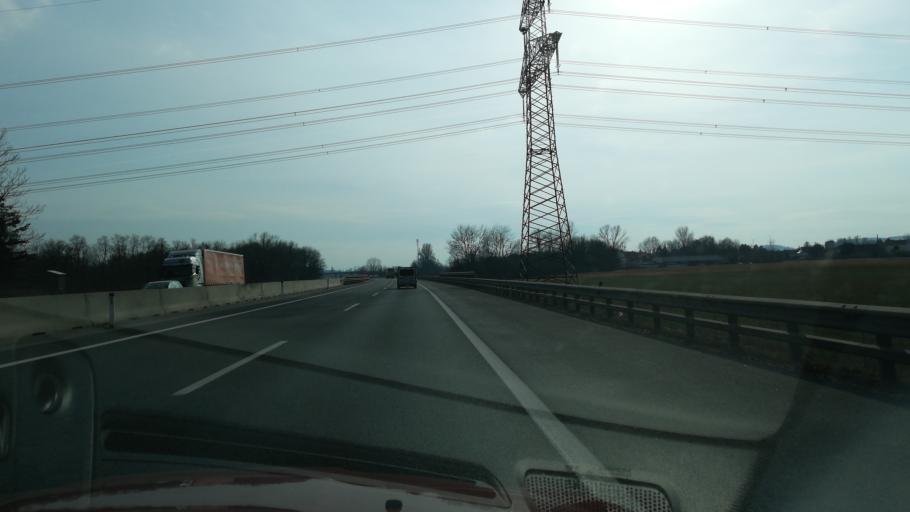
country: AT
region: Lower Austria
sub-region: Politischer Bezirk Sankt Polten
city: Traismauer
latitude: 48.3289
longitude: 15.7203
